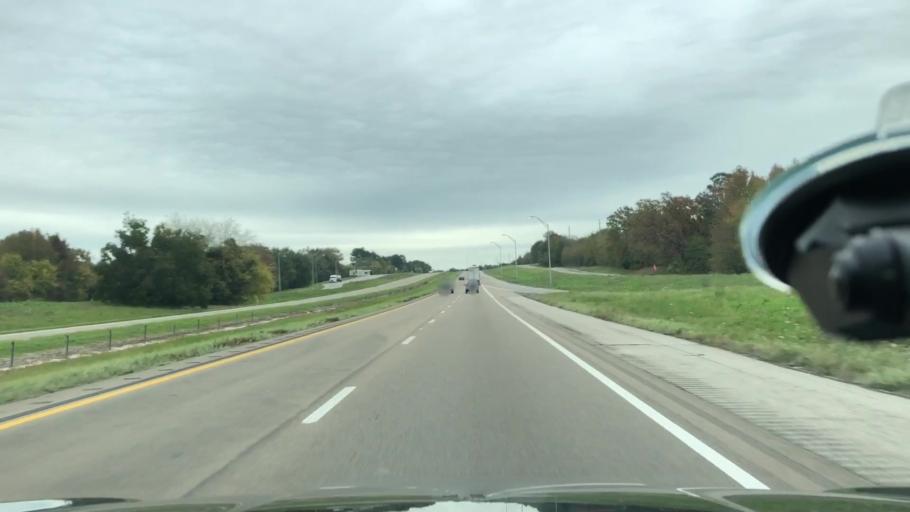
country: US
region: Texas
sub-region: Titus County
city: Mount Pleasant
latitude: 33.1585
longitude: -95.0488
